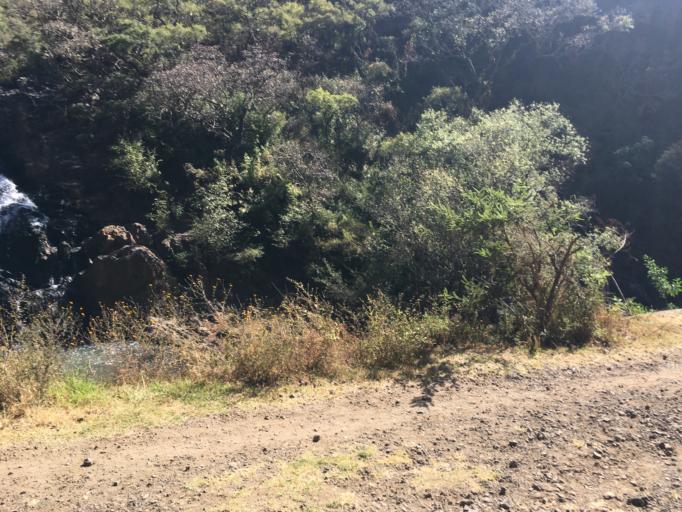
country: MX
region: Michoacan
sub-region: Morelia
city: Montana Monarca (Punta Altozano)
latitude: 19.6770
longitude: -101.1538
